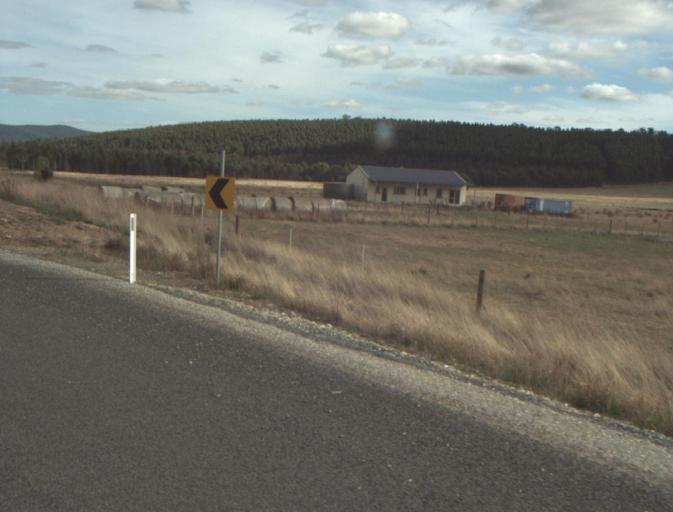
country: AU
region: Tasmania
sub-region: Launceston
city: Mayfield
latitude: -41.1979
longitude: 147.1808
